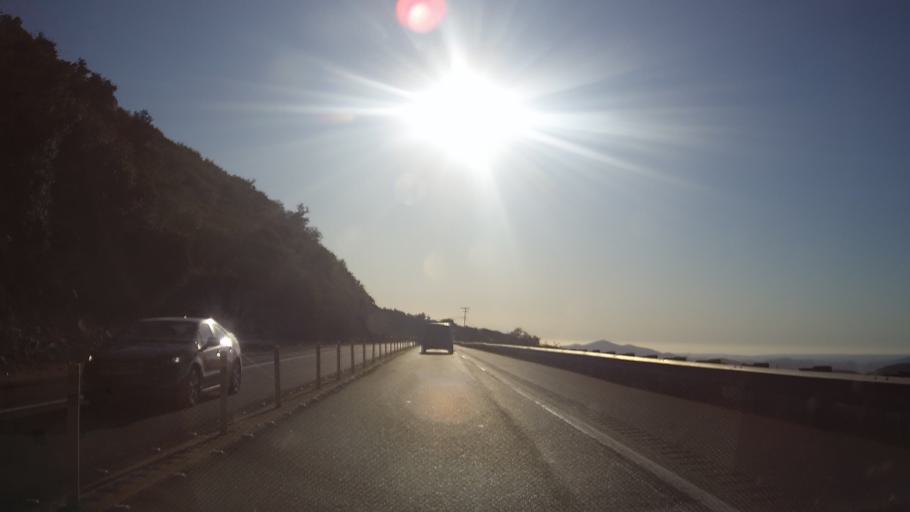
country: US
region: California
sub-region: San Diego County
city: Poway
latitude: 32.9962
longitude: -116.9719
